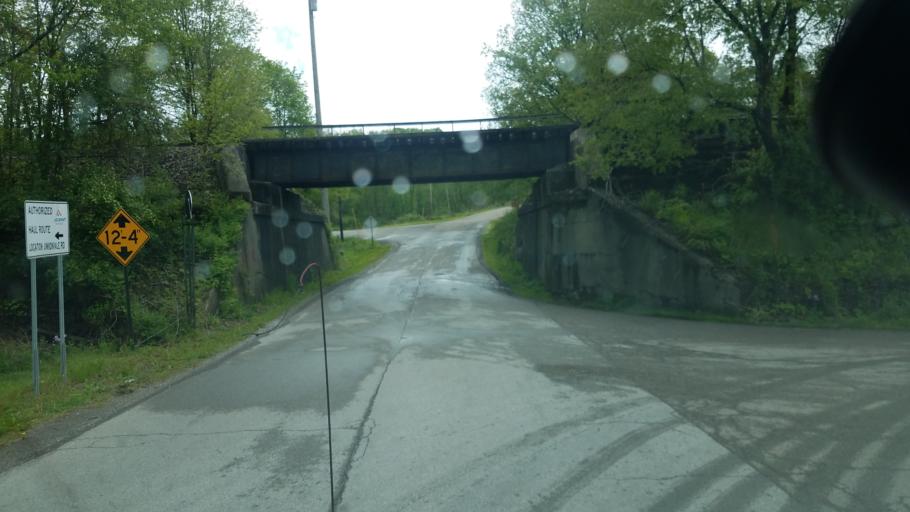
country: US
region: Ohio
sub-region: Harrison County
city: Cadiz
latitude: 40.2722
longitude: -80.9272
